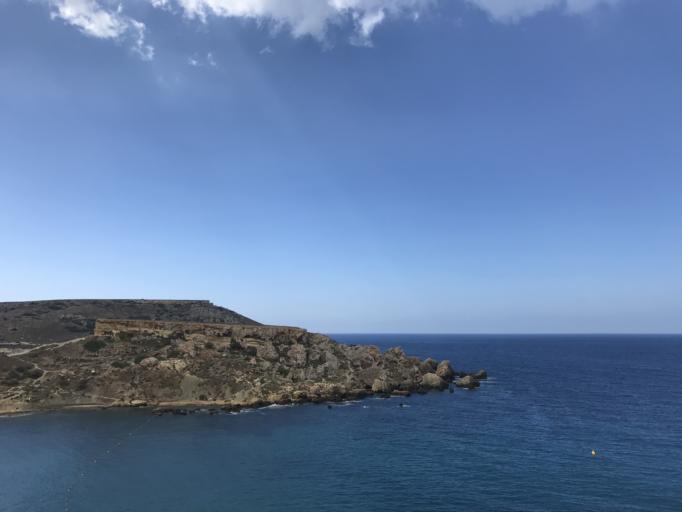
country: MT
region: L-Imgarr
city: Imgarr
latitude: 35.9307
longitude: 14.3435
